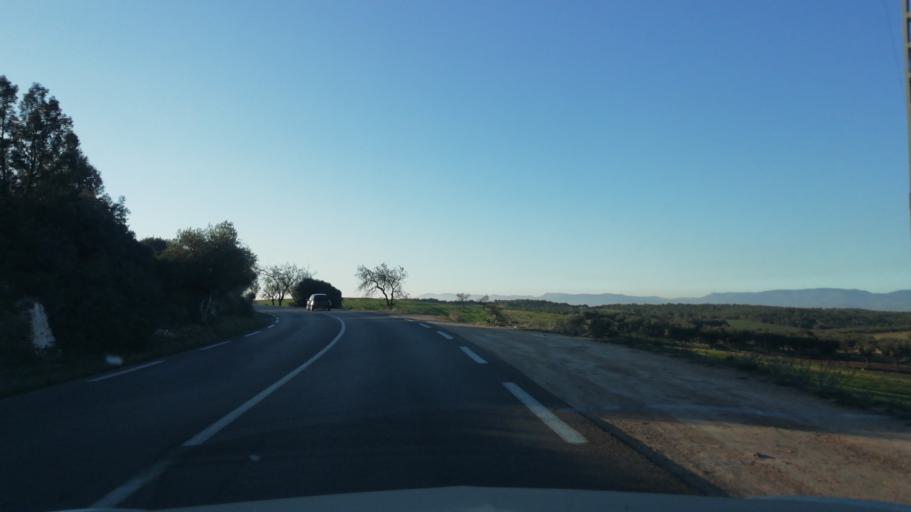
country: DZ
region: Tlemcen
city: Beni Mester
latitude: 34.8270
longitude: -1.5995
